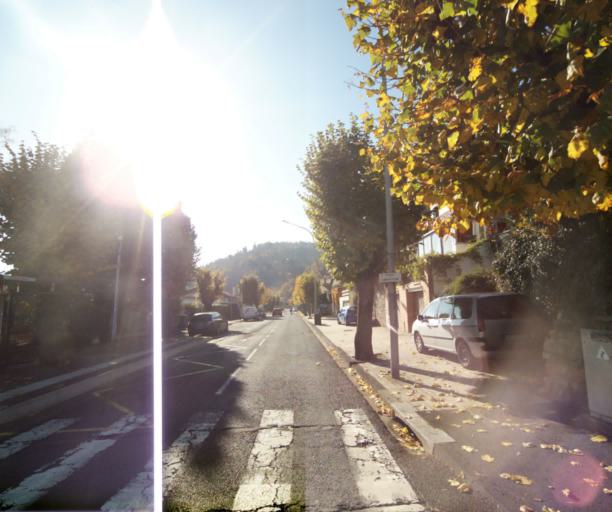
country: FR
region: Auvergne
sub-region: Departement du Puy-de-Dome
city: Ceyrat
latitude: 45.7288
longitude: 3.0642
